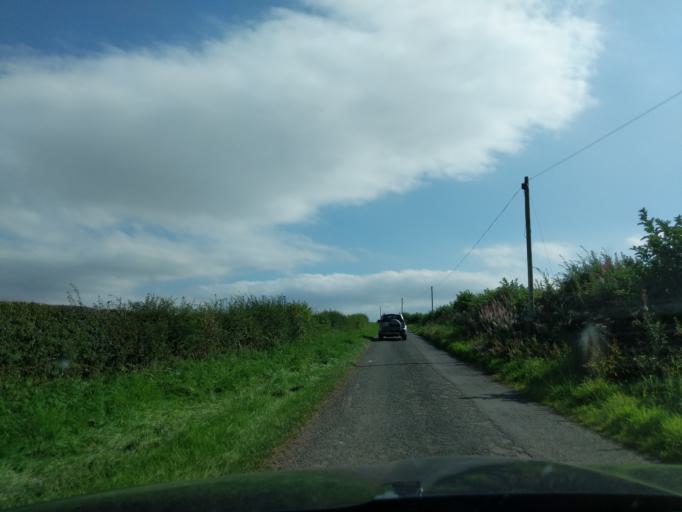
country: GB
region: England
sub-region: Northumberland
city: Ford
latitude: 55.6553
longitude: -2.1491
